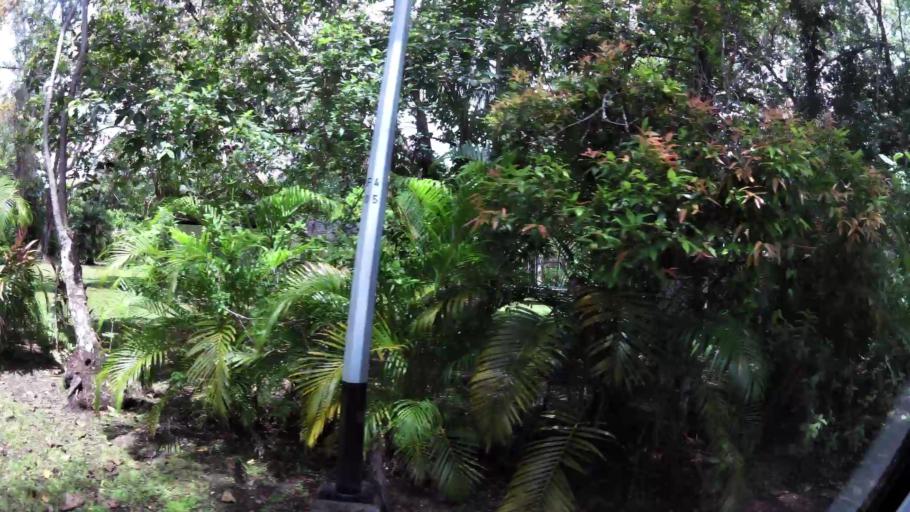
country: BN
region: Belait
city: Kuala Belait
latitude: 4.5974
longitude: 114.2682
